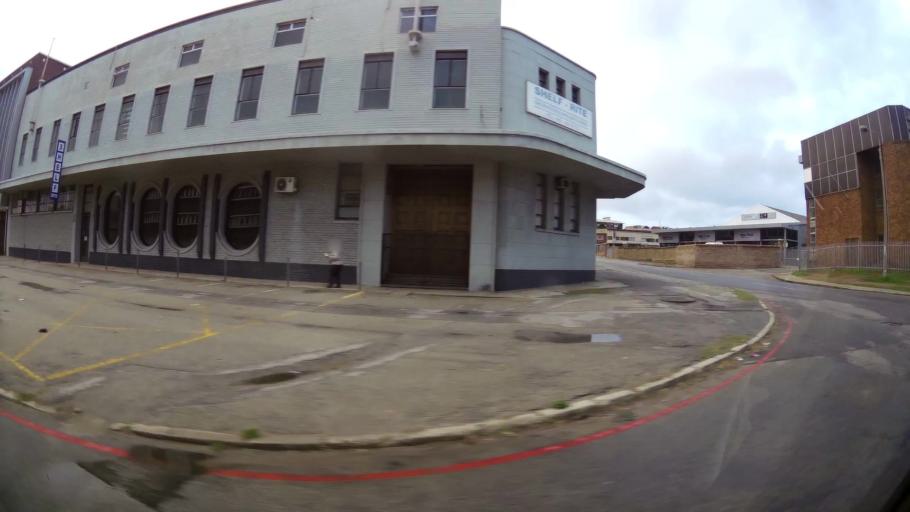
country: ZA
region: Eastern Cape
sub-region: Nelson Mandela Bay Metropolitan Municipality
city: Port Elizabeth
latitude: -33.9326
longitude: 25.6045
